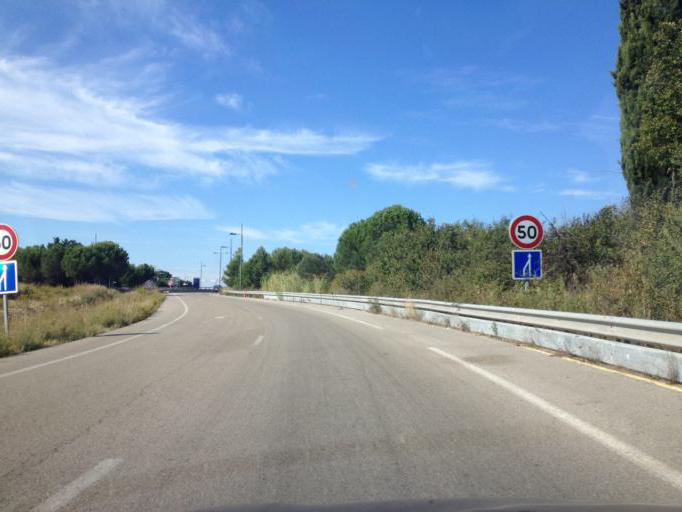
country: FR
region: Languedoc-Roussillon
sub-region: Departement de l'Herault
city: Le Cres
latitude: 43.6080
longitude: 3.9337
